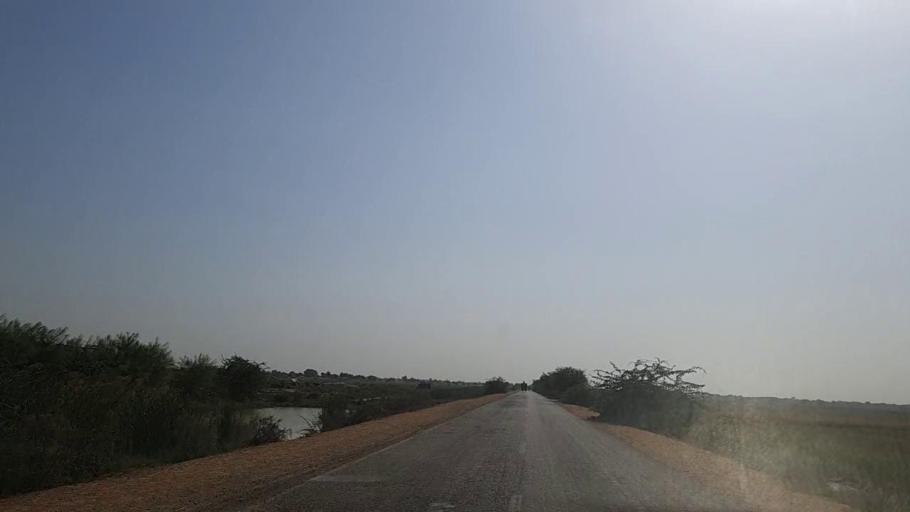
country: PK
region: Sindh
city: Mirpur Batoro
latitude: 24.5842
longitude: 68.2901
